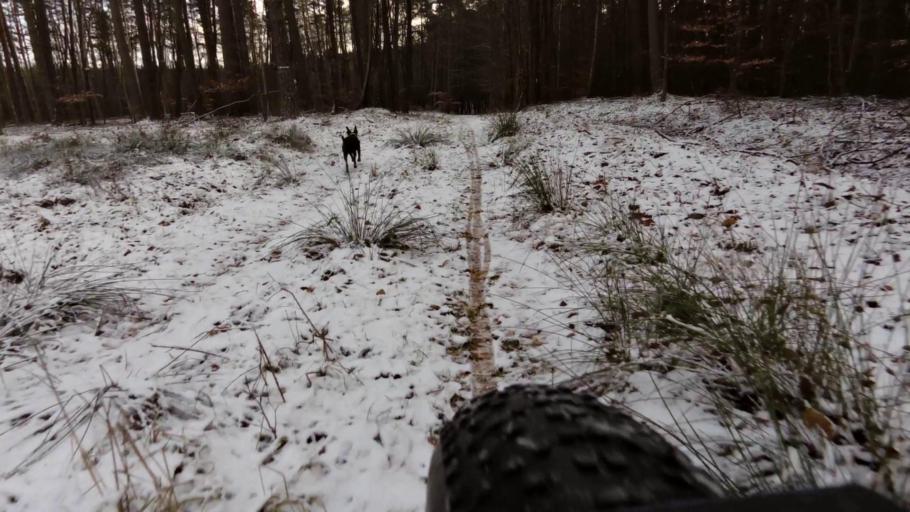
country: PL
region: West Pomeranian Voivodeship
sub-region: Powiat walecki
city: Tuczno
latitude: 53.2943
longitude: 16.2929
